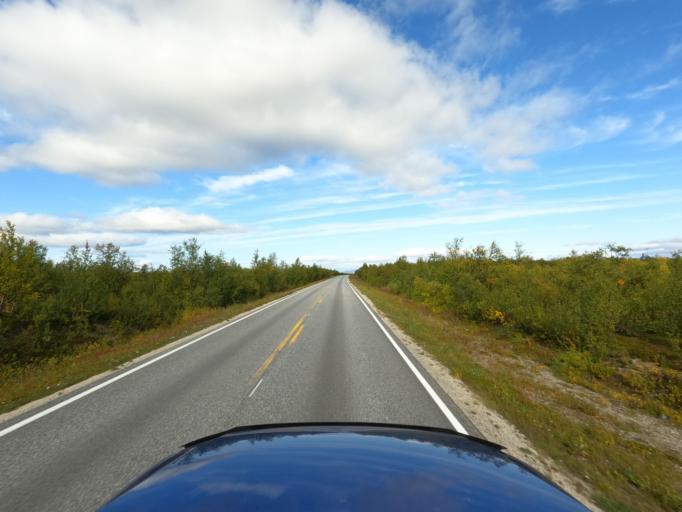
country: NO
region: Finnmark Fylke
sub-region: Karasjok
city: Karasjohka
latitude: 69.6538
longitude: 25.2784
